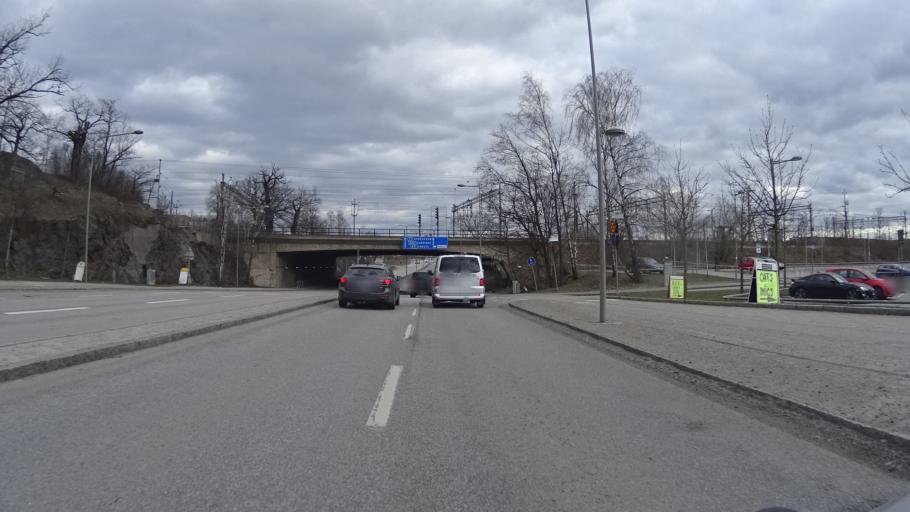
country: SE
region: Stockholm
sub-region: Huddinge Kommun
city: Huddinge
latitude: 59.2777
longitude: 18.0069
